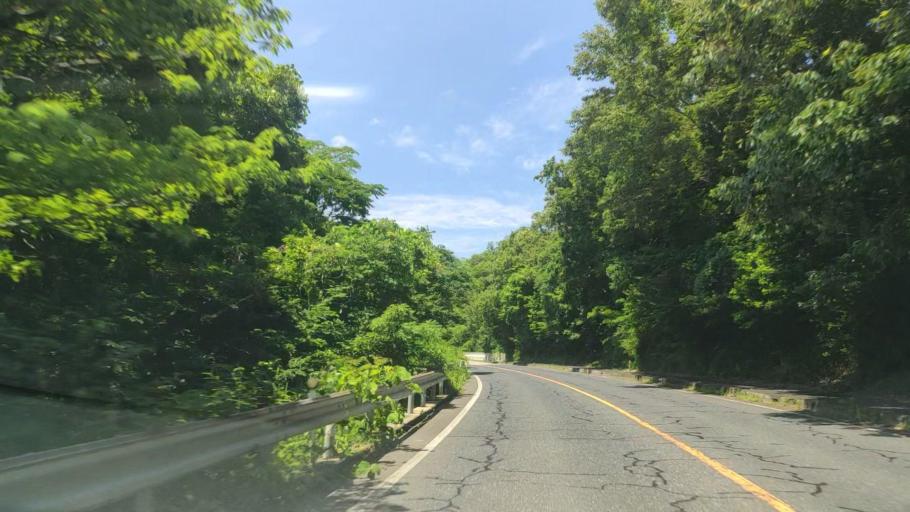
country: JP
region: Tottori
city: Tottori
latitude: 35.5276
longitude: 134.2301
